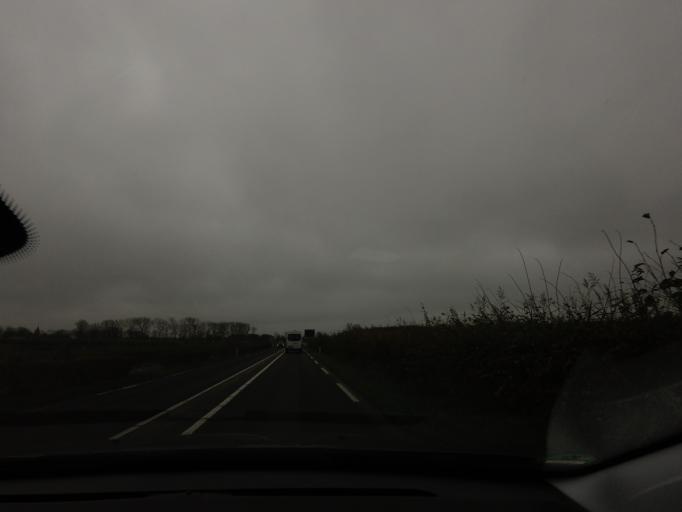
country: NL
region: Zeeland
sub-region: Schouwen-Duiveland
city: Renesse
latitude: 51.7041
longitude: 3.8085
